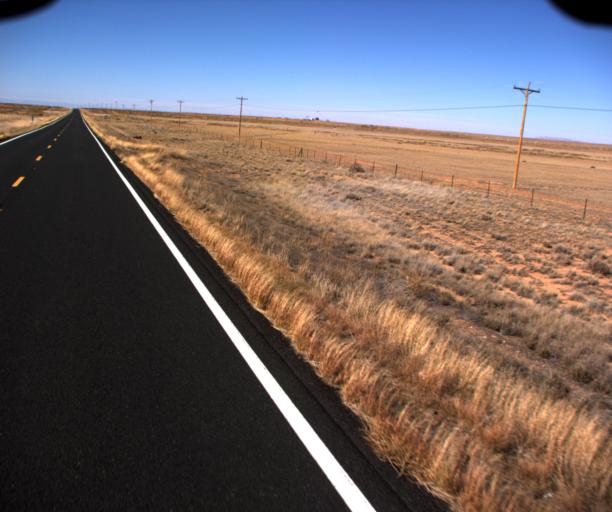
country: US
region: Arizona
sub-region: Coconino County
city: Tuba City
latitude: 36.0002
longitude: -111.0358
